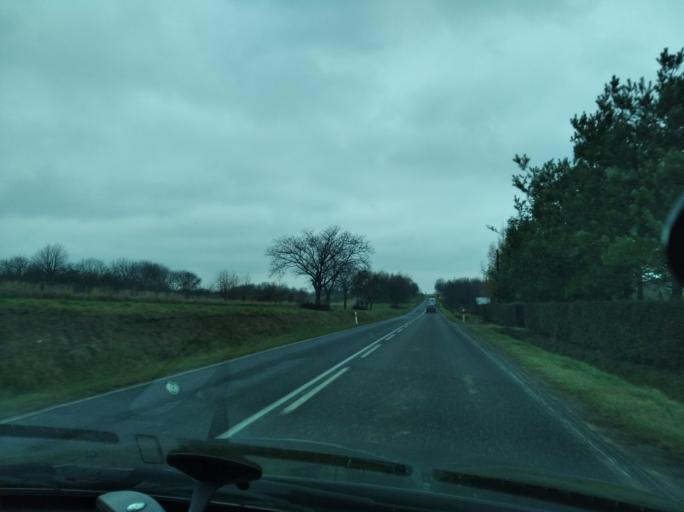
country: PL
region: Subcarpathian Voivodeship
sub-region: Powiat przeworski
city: Sietesz
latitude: 49.9971
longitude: 22.3669
